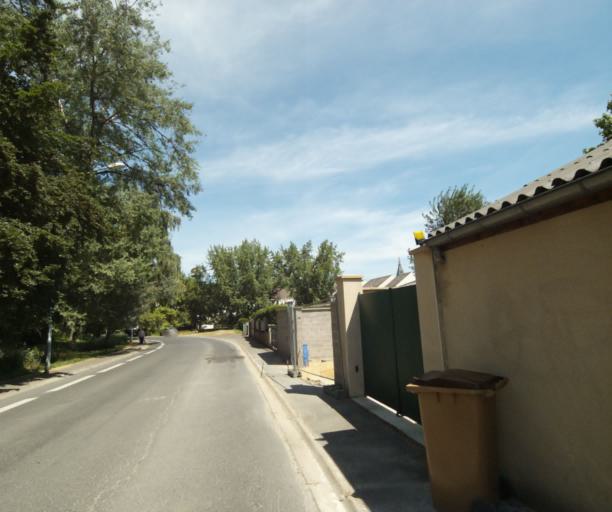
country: FR
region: Champagne-Ardenne
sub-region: Departement des Ardennes
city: Charleville-Mezieres
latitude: 49.7575
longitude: 4.7115
